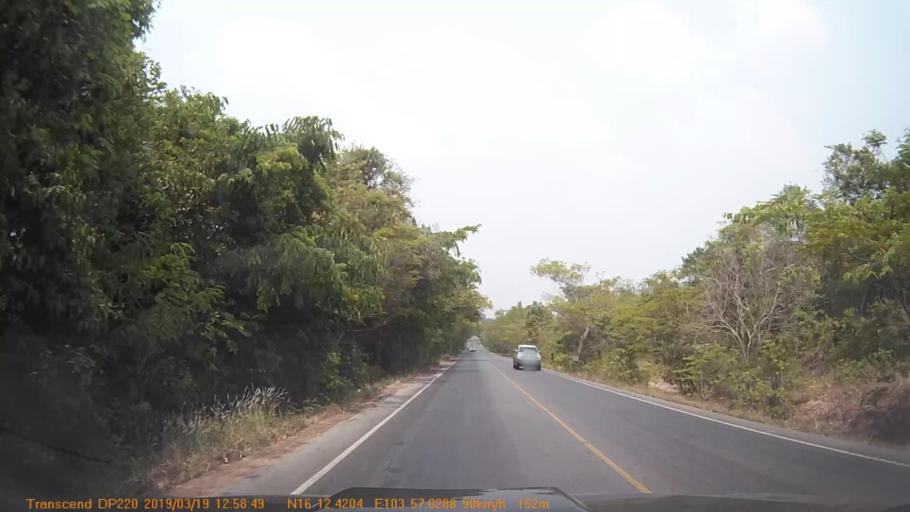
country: TH
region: Roi Et
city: Waeng
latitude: 16.2074
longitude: 103.9506
